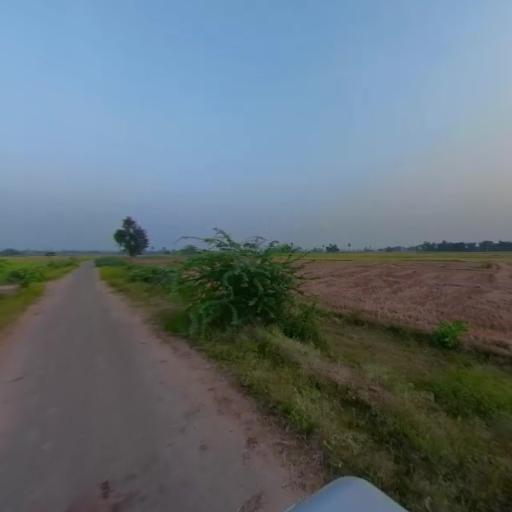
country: IN
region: Telangana
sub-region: Nalgonda
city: Suriapet
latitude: 17.0765
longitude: 79.5491
